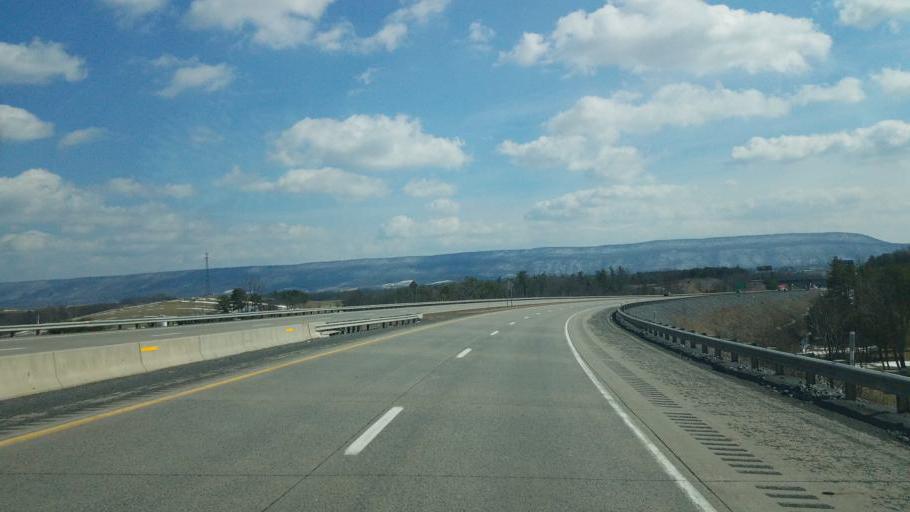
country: US
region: Pennsylvania
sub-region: Mifflin County
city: Milroy
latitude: 40.7293
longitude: -77.6060
